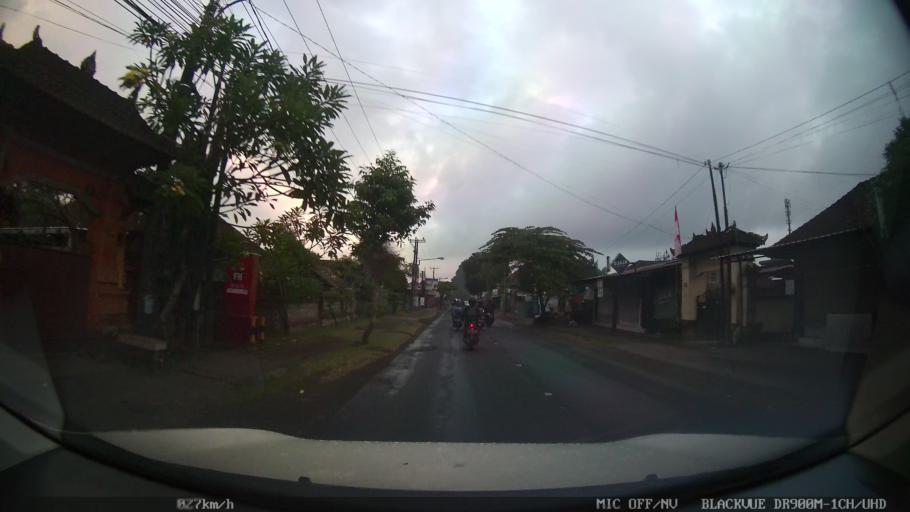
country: ID
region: Bali
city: Banjar Parekan
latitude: -8.5694
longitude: 115.2196
